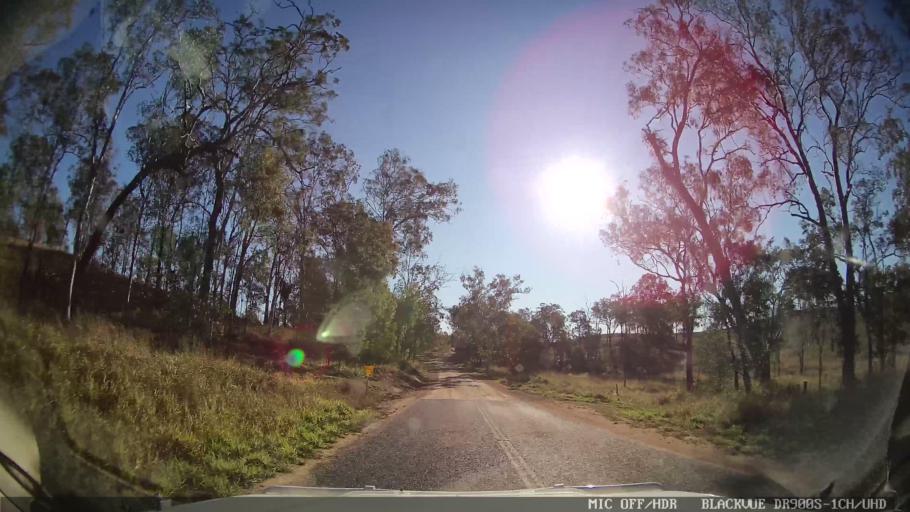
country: AU
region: Queensland
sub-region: Bundaberg
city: Sharon
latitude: -24.8032
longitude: 151.6482
